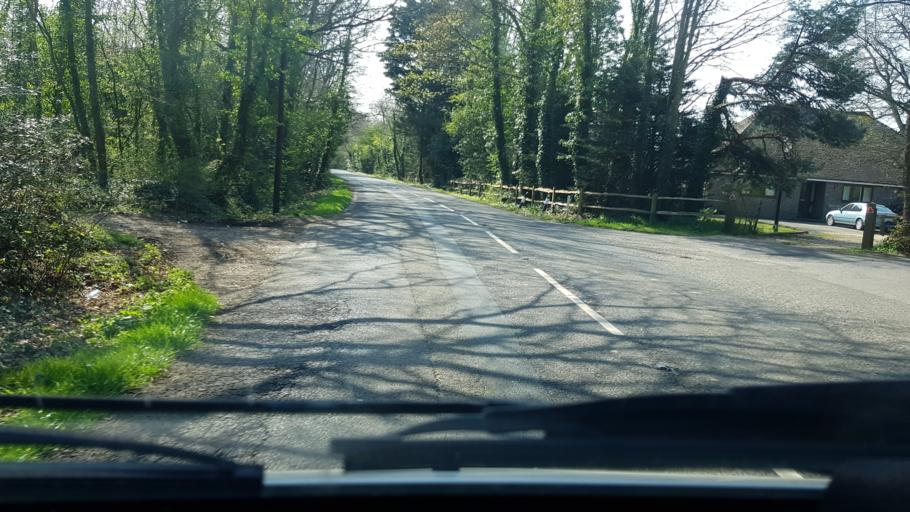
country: GB
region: England
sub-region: West Sussex
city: Chichester
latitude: 50.8504
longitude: -0.8104
